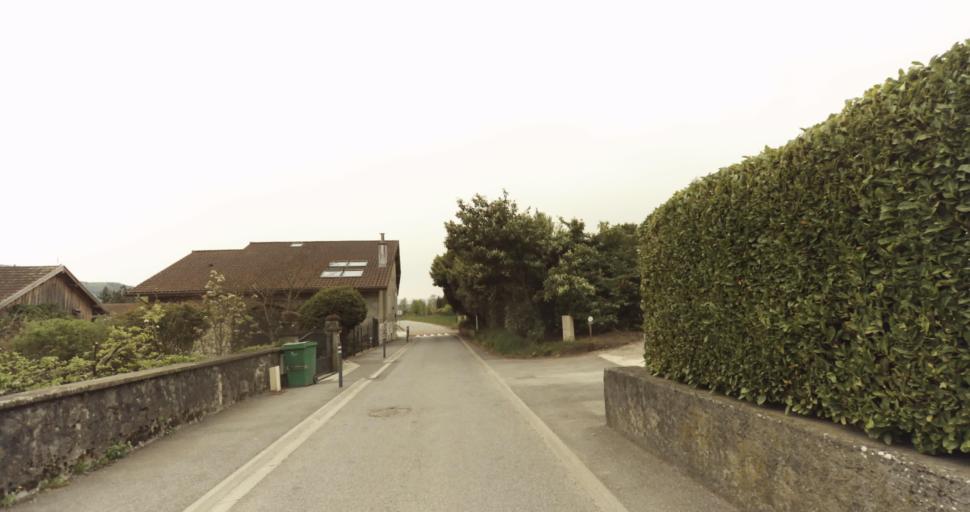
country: FR
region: Rhone-Alpes
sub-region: Departement de l'Isere
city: Montbonnot-Saint-Martin
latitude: 45.2286
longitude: 5.8173
